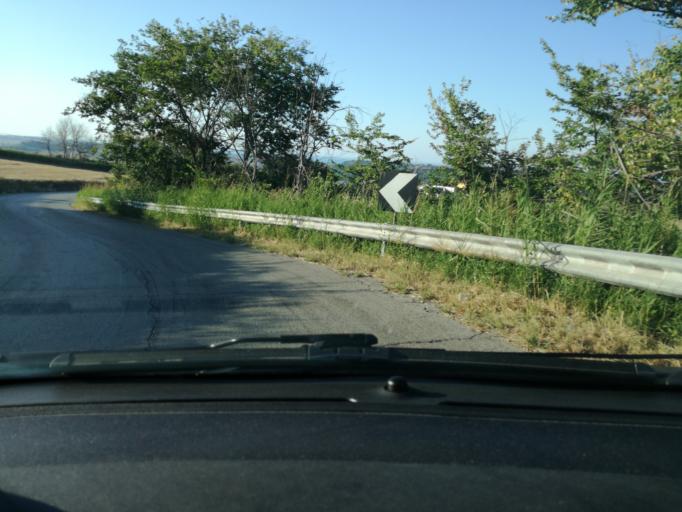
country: IT
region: Molise
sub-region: Provincia di Campobasso
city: Guglionesi
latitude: 41.9294
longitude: 14.9300
